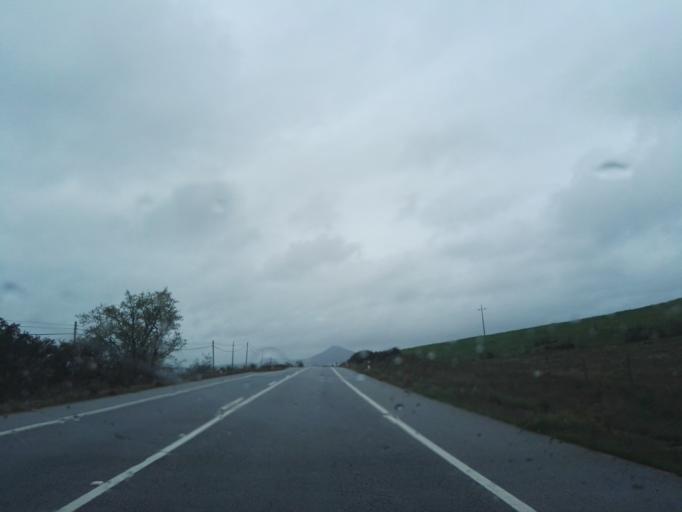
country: PT
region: Portalegre
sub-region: Portalegre
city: Urra
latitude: 39.2472
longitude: -7.4017
